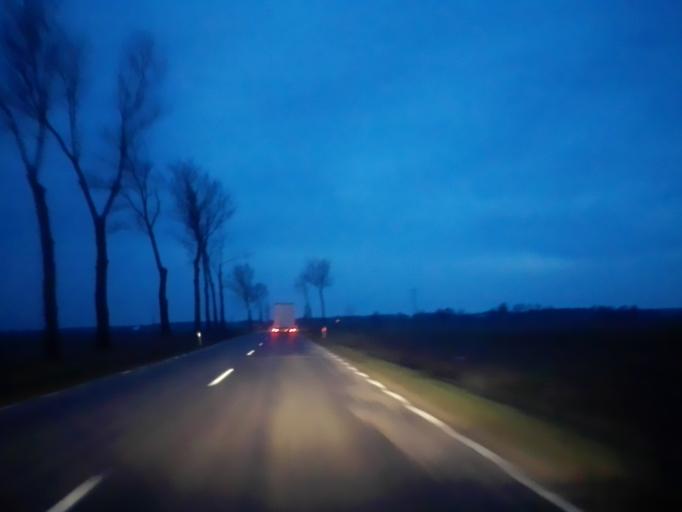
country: PL
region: Podlasie
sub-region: Powiat lomzynski
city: Sniadowo
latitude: 53.0795
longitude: 22.0178
